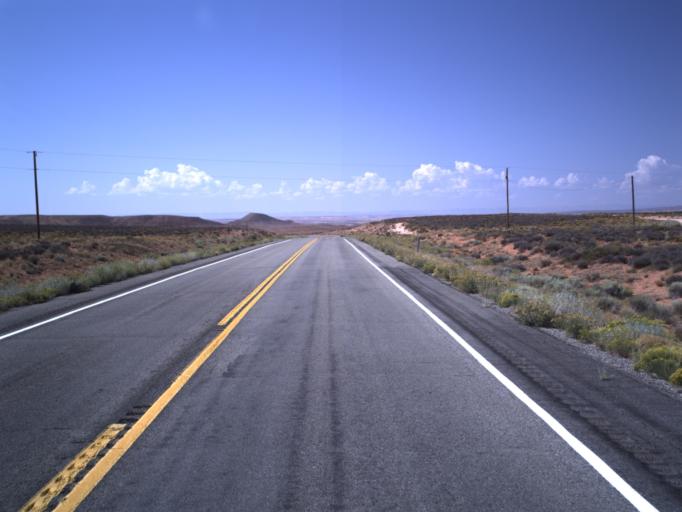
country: US
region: Utah
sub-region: San Juan County
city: Blanding
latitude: 37.0185
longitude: -109.6086
